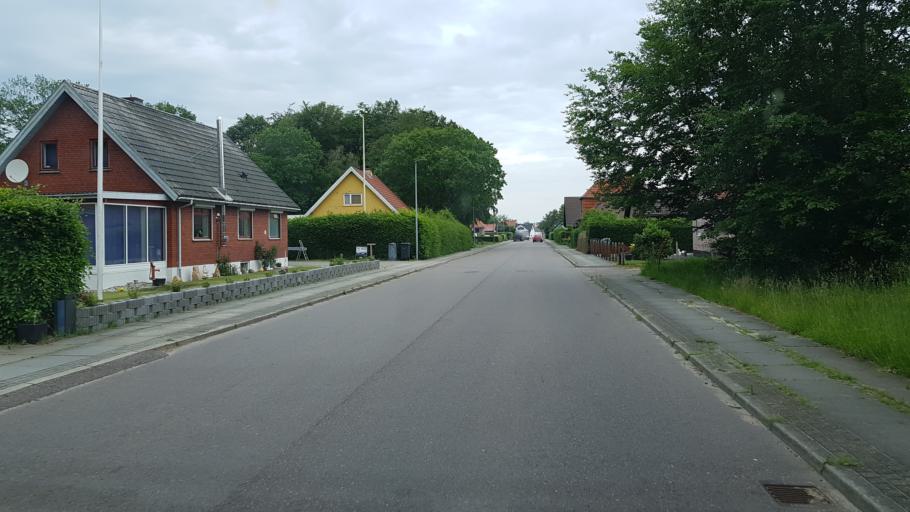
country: DK
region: South Denmark
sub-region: Varde Kommune
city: Oksbol
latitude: 55.6524
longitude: 8.2899
